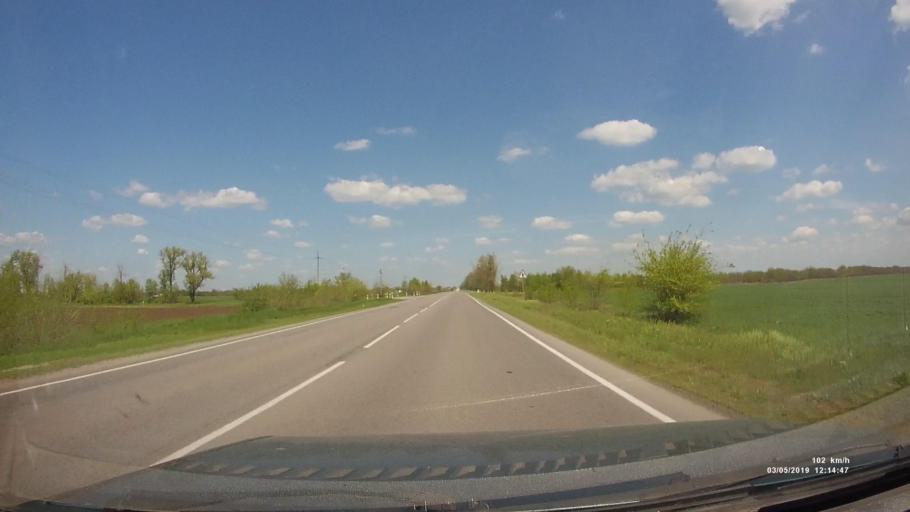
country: RU
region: Rostov
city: Melikhovskaya
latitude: 47.3488
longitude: 40.5670
